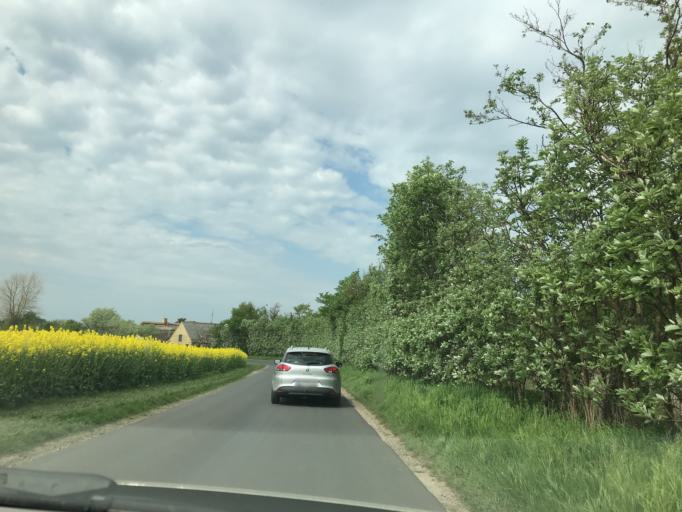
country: DK
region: South Denmark
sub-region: Assens Kommune
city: Assens
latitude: 55.3329
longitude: 9.8974
